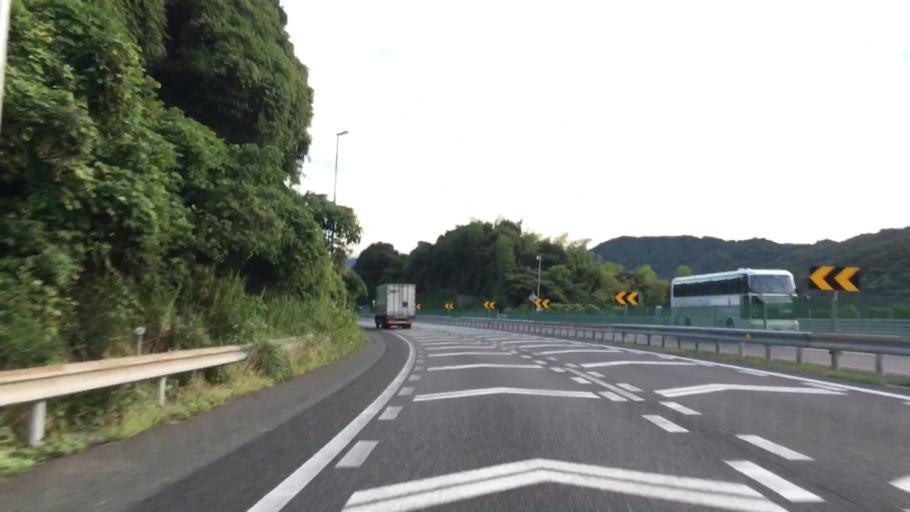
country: JP
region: Yamaguchi
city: Shimonoseki
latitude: 34.0345
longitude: 130.9632
